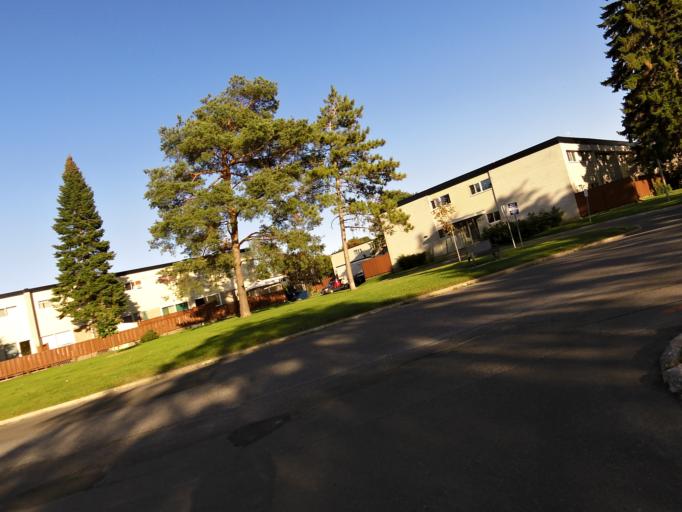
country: CA
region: Ontario
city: Ottawa
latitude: 45.3603
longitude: -75.7174
